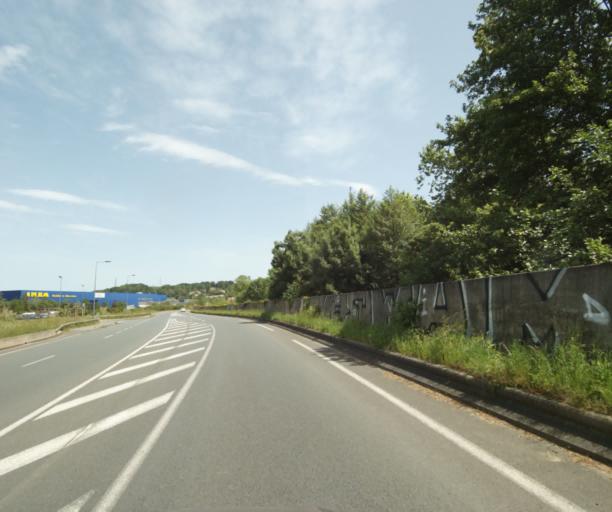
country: FR
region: Aquitaine
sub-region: Departement des Pyrenees-Atlantiques
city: Mouguerre
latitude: 43.4763
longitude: -1.4482
